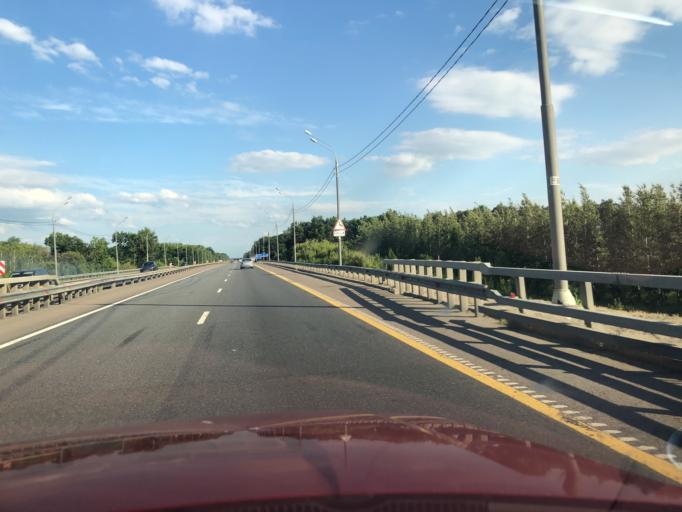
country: RU
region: Lipetsk
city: Zadonsk
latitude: 52.4242
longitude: 38.8318
